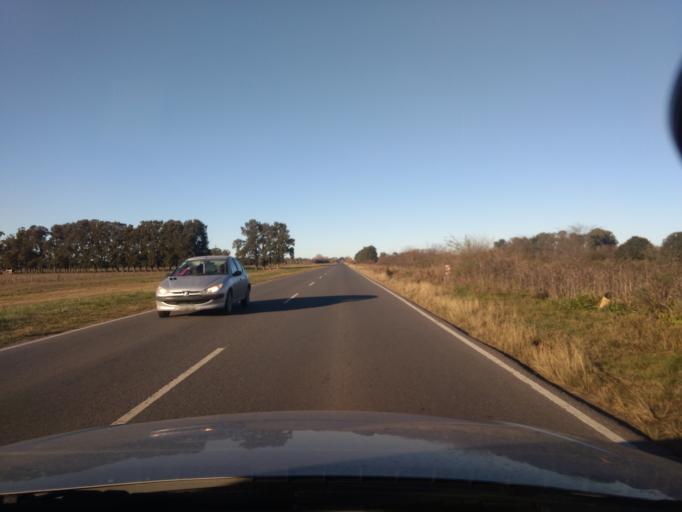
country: AR
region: Buenos Aires
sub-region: Partido de Lujan
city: Lujan
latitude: -34.6046
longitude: -59.1054
